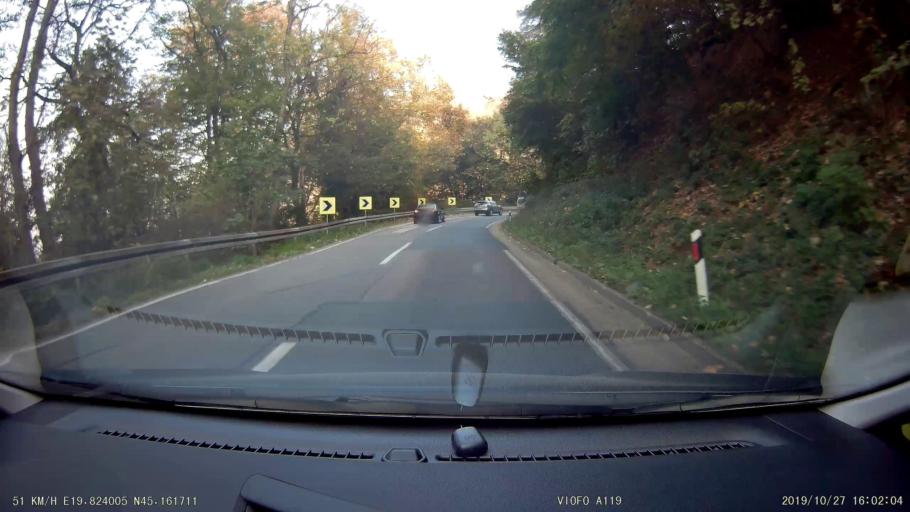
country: RS
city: Vrdnik
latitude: 45.1618
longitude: 19.8242
